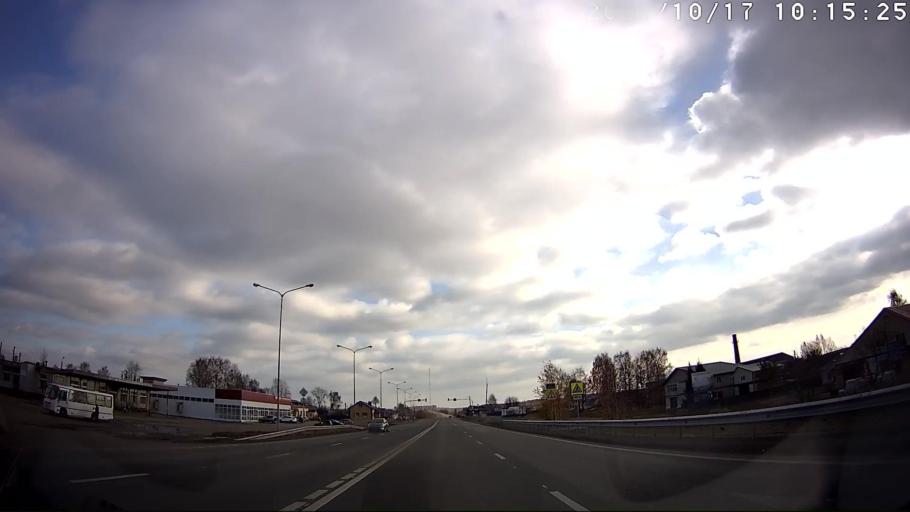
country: RU
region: Mariy-El
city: Sovetskiy
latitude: 56.7521
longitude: 48.4783
